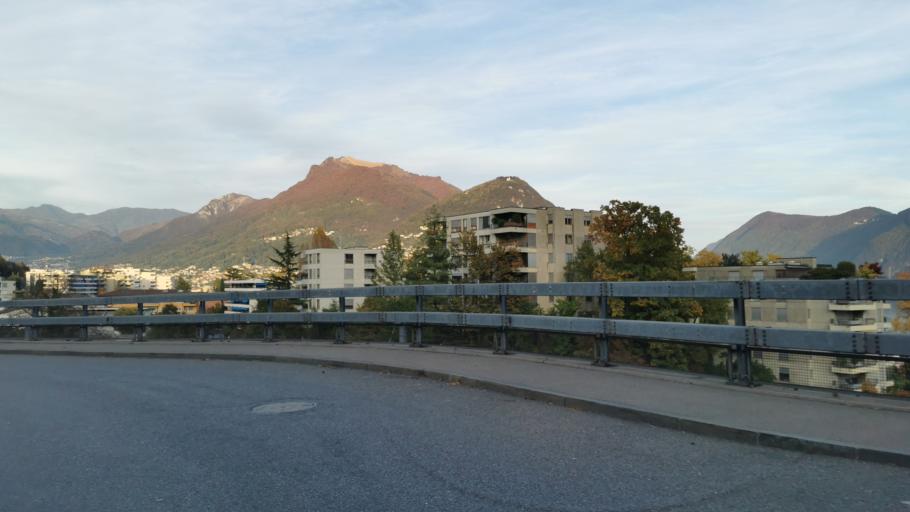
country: CH
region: Ticino
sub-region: Lugano District
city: Sorengo
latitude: 45.9949
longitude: 8.9420
